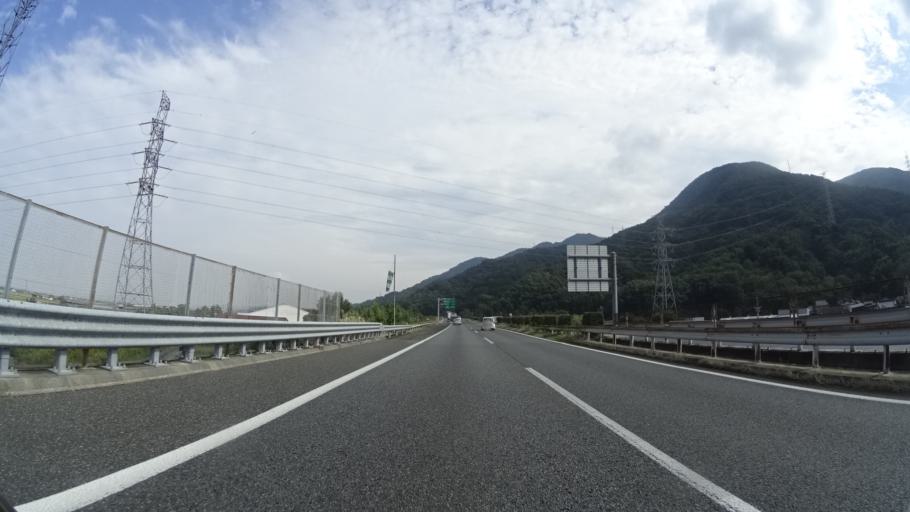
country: JP
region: Kumamoto
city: Yatsushiro
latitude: 32.5210
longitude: 130.6556
